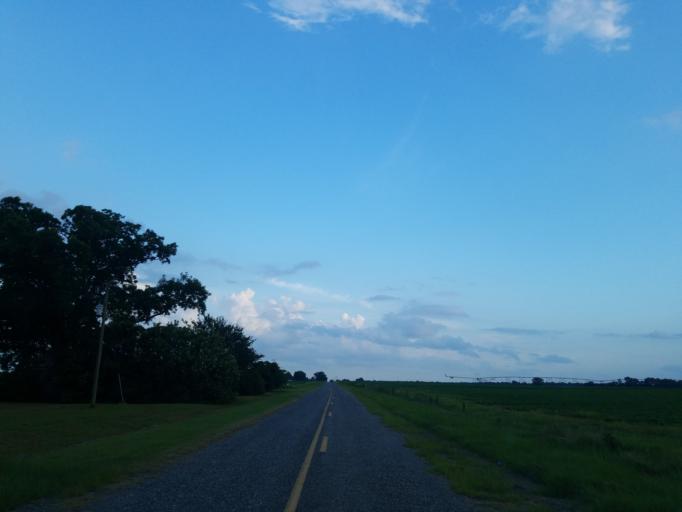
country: US
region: Georgia
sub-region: Dooly County
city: Unadilla
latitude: 32.1729
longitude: -83.7209
